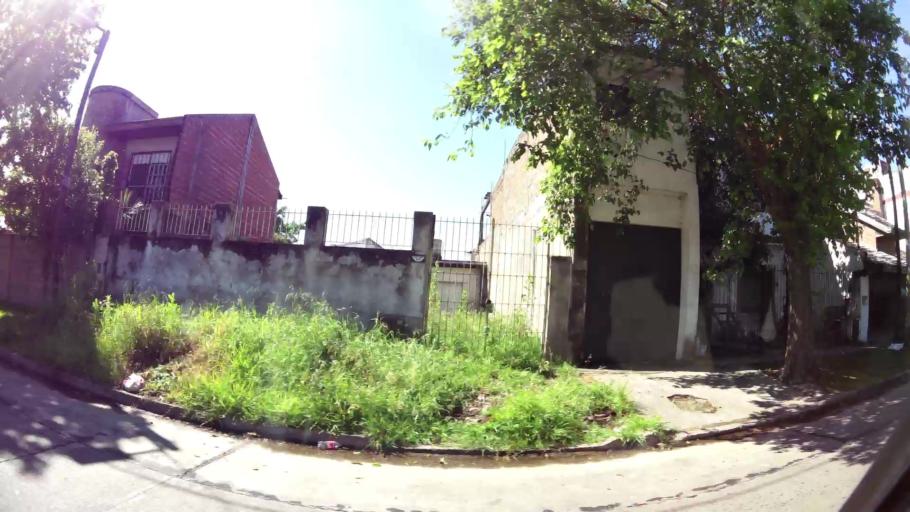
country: AR
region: Buenos Aires
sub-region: Partido de Quilmes
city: Quilmes
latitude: -34.6978
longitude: -58.2977
